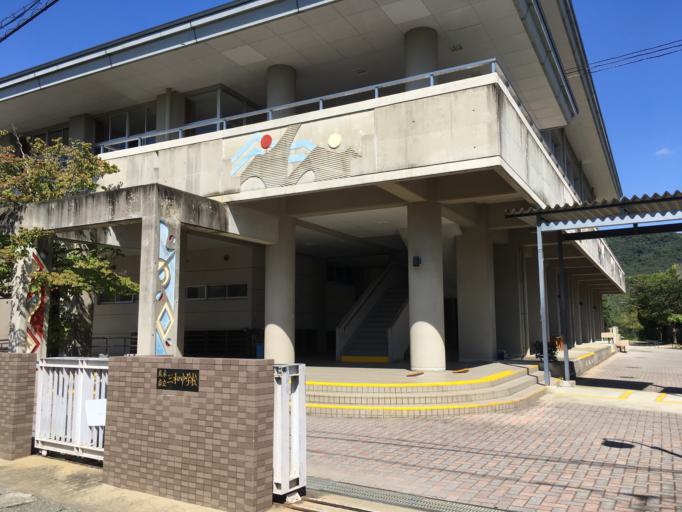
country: JP
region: Kumamoto
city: Kumamoto
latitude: 32.7862
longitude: 130.6647
